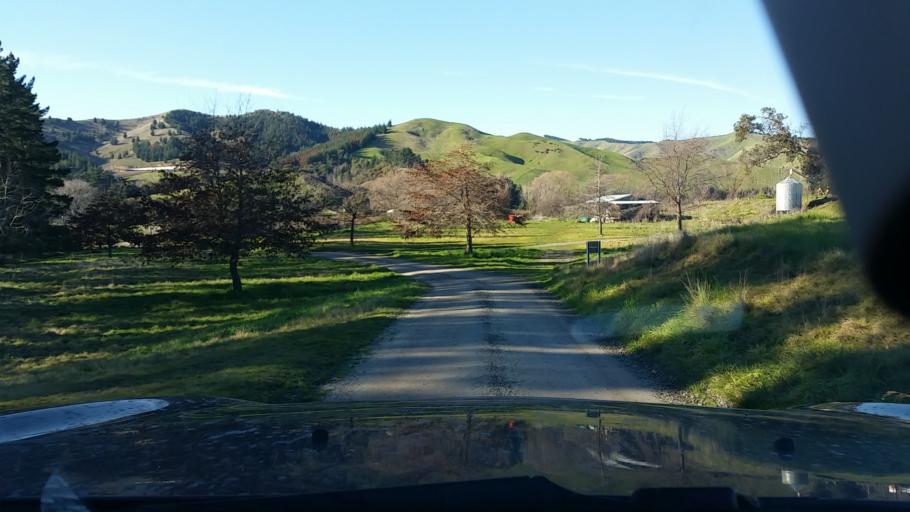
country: NZ
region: Marlborough
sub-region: Marlborough District
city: Blenheim
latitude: -41.5620
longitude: 173.9257
